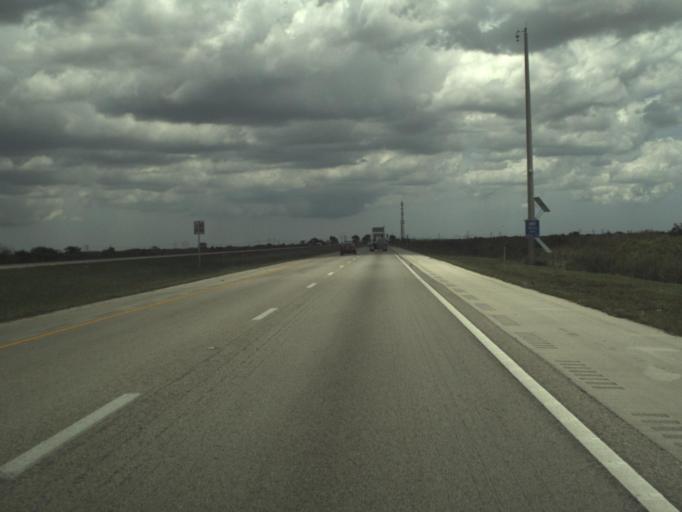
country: US
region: Florida
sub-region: Broward County
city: Weston
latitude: 26.1459
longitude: -80.4861
